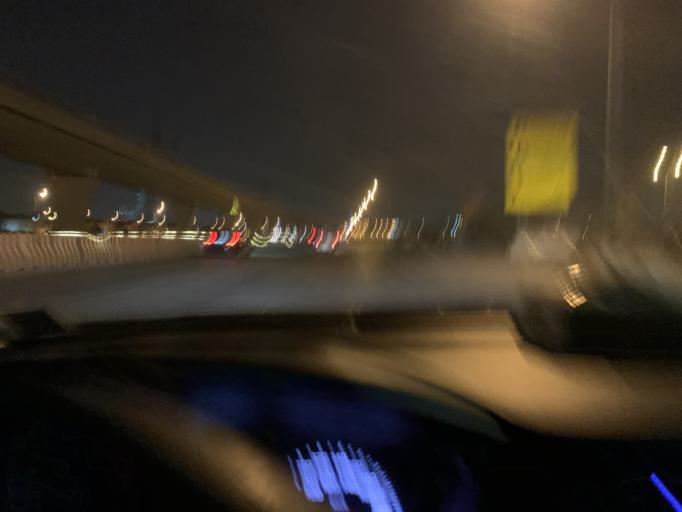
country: SA
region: Ar Riyad
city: Riyadh
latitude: 24.7910
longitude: 46.6707
